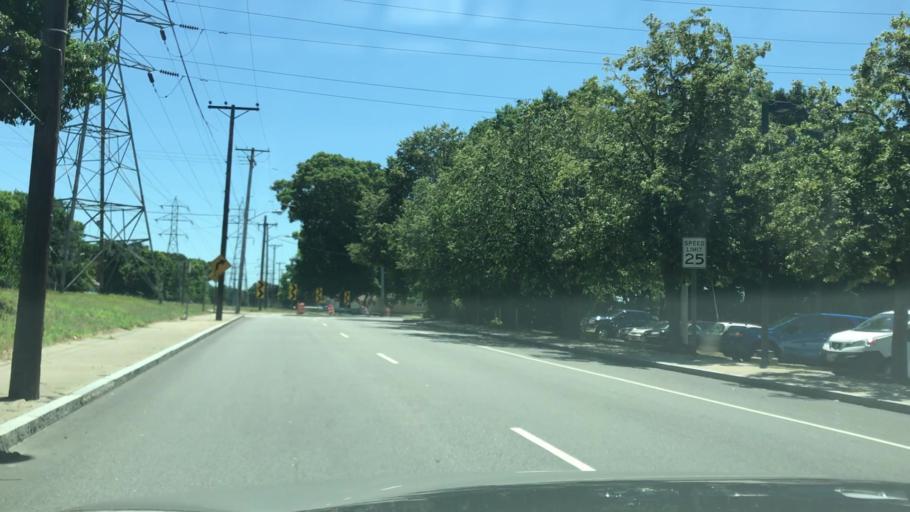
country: US
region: Rhode Island
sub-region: Providence County
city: Pawtucket
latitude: 41.8664
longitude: -71.3762
